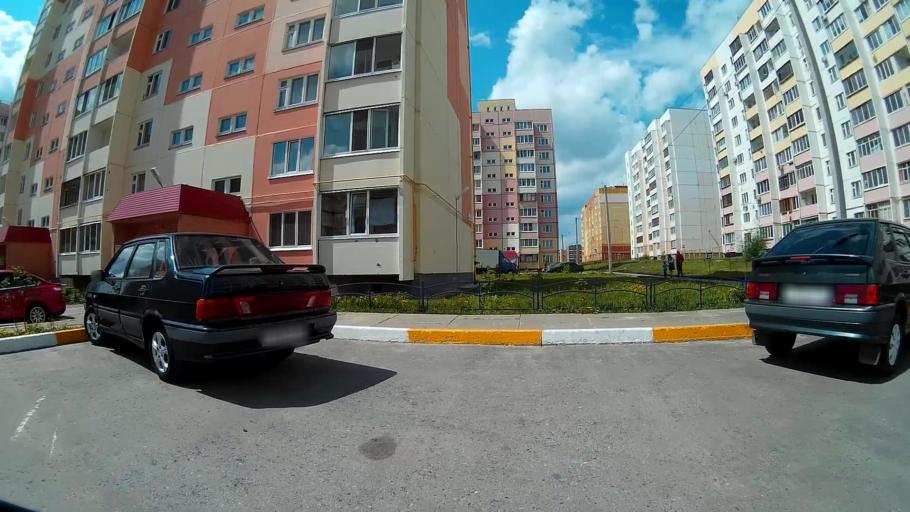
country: RU
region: Ulyanovsk
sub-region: Ulyanovskiy Rayon
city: Ulyanovsk
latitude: 54.3481
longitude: 48.3462
